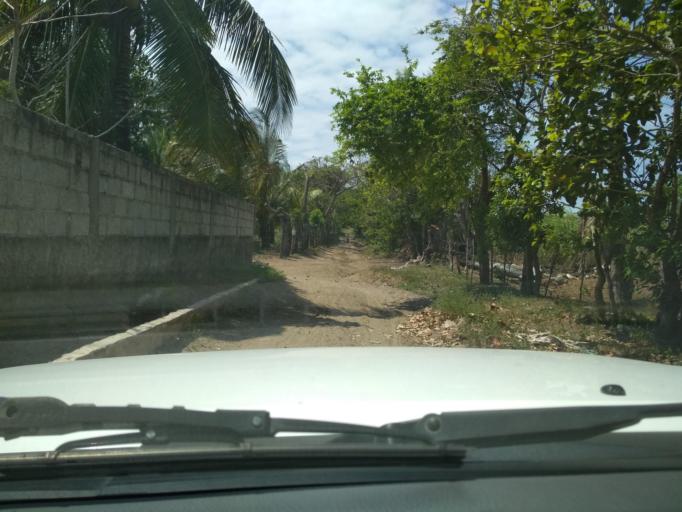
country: MX
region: Veracruz
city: Anton Lizardo
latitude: 19.0082
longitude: -95.9901
